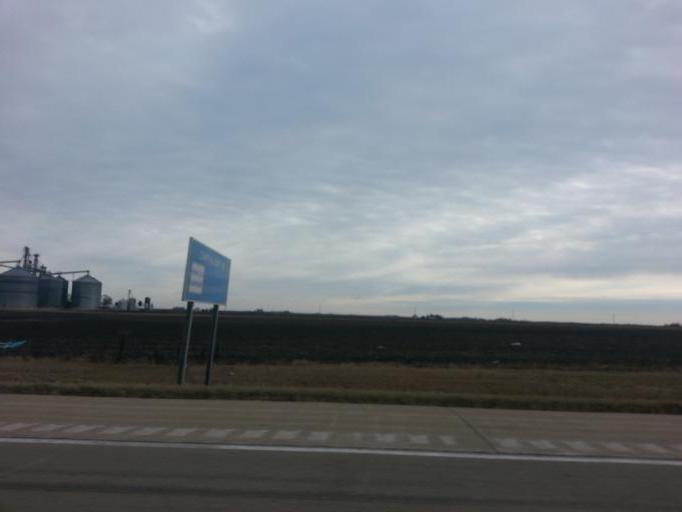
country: US
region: Illinois
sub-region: Woodford County
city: El Paso
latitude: 40.7044
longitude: -89.0292
